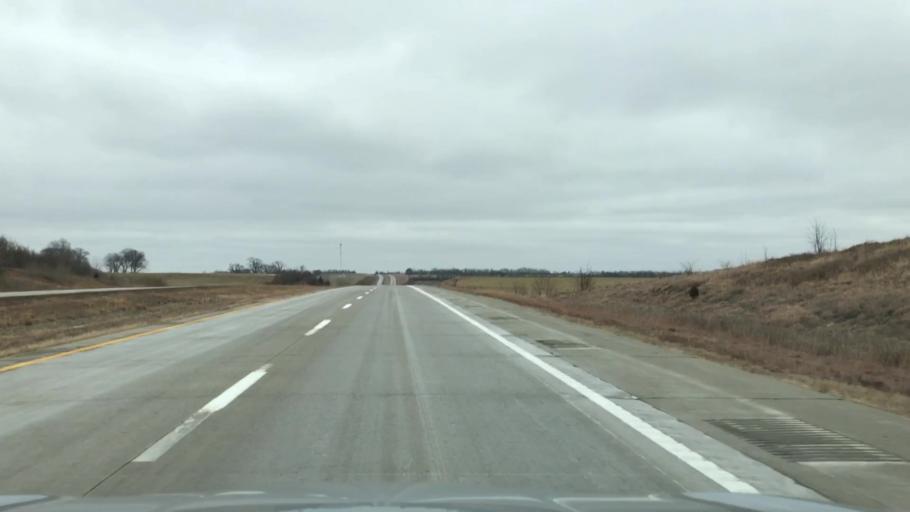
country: US
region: Missouri
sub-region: Caldwell County
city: Hamilton
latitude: 39.7349
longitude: -93.7923
